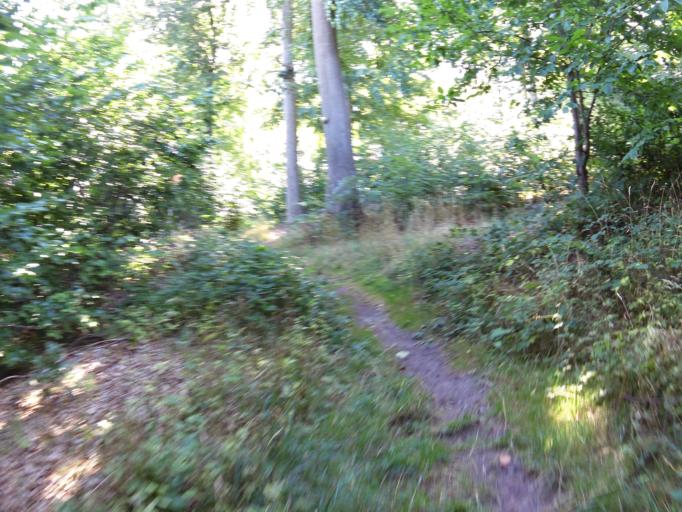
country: DE
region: Mecklenburg-Vorpommern
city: Seebad Bansin
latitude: 53.9732
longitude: 14.1413
